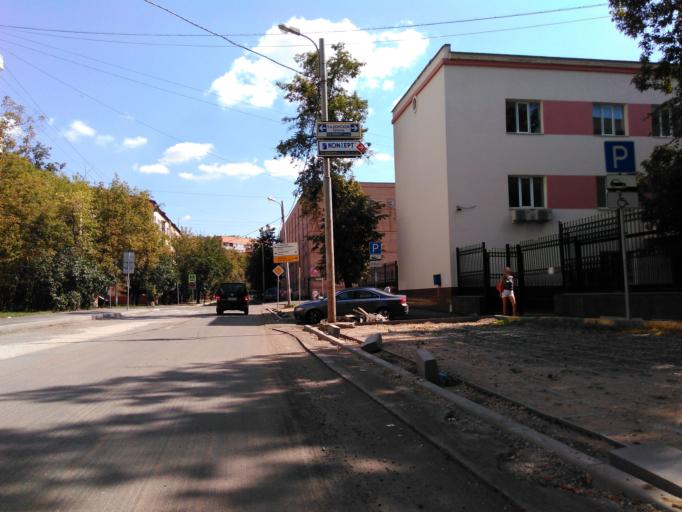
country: RU
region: Moscow
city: Novyye Cheremushki
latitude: 55.7088
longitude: 37.5985
